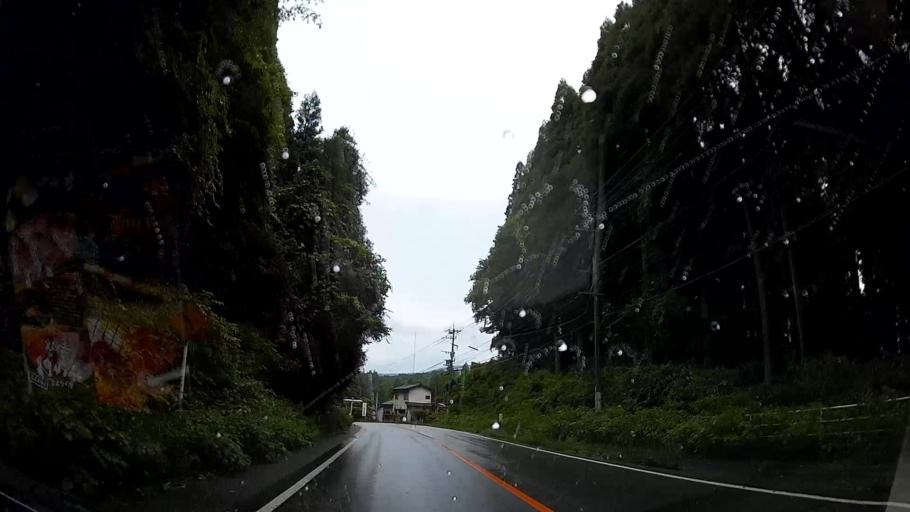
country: JP
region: Oita
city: Tsukawaki
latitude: 33.1425
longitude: 131.0611
